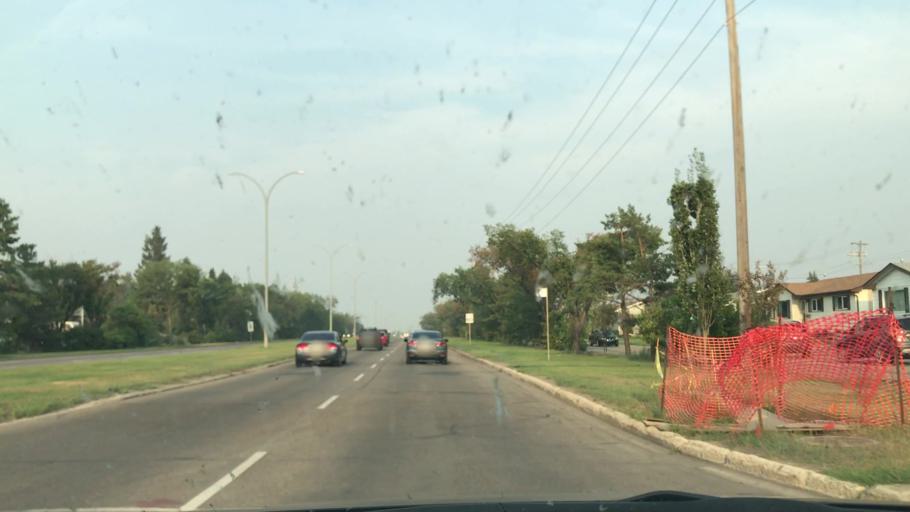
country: CA
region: Alberta
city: Edmonton
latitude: 53.5996
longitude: -113.4553
